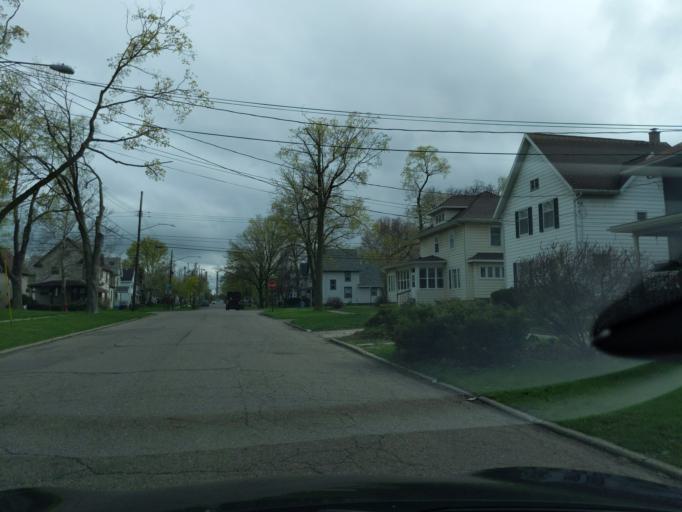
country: US
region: Michigan
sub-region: Ingham County
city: Lansing
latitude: 42.7427
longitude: -84.5585
